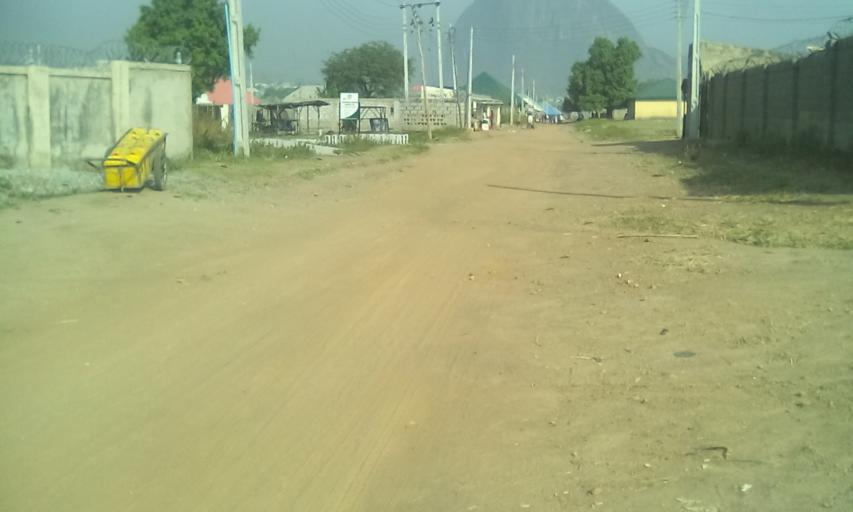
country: NG
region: Abuja Federal Capital Territory
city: Madala
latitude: 9.1066
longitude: 7.2424
